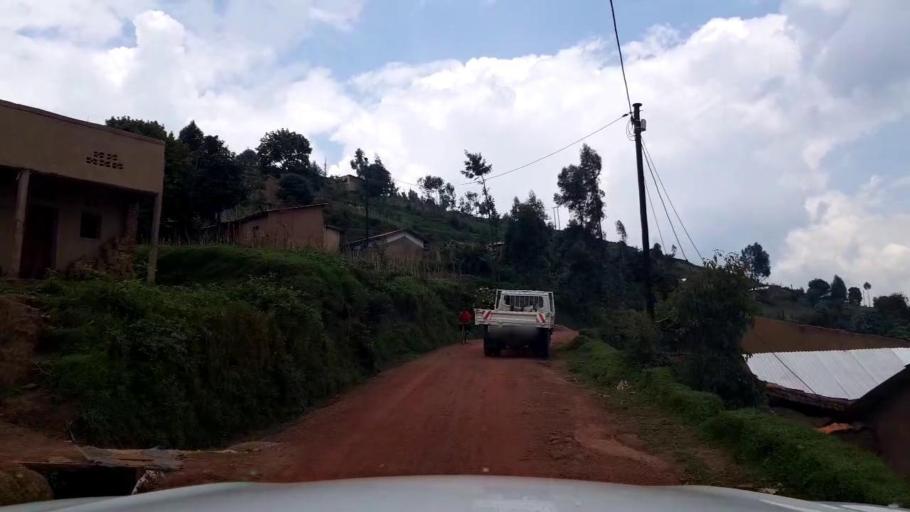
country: RW
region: Northern Province
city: Byumba
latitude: -1.5261
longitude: 29.9564
